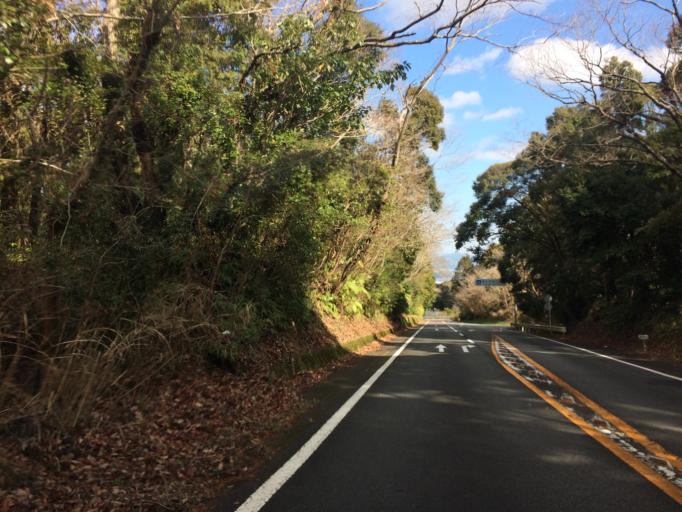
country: JP
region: Shizuoka
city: Shizuoka-shi
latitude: 34.9771
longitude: 138.4471
